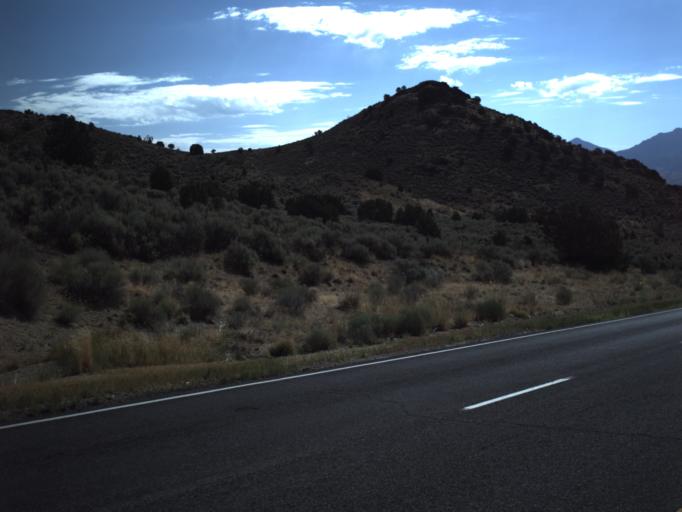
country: US
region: Utah
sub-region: Utah County
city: Genola
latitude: 39.9528
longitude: -112.0303
